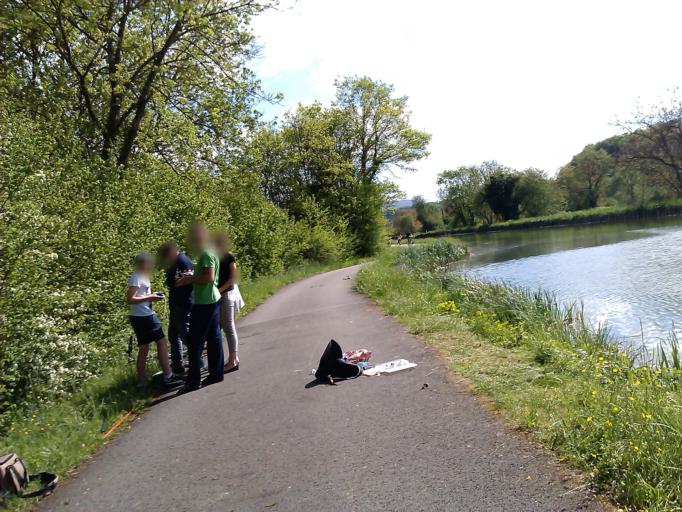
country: FR
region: Franche-Comte
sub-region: Departement du Doubs
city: Colombier-Fontaine
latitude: 47.4413
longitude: 6.6288
